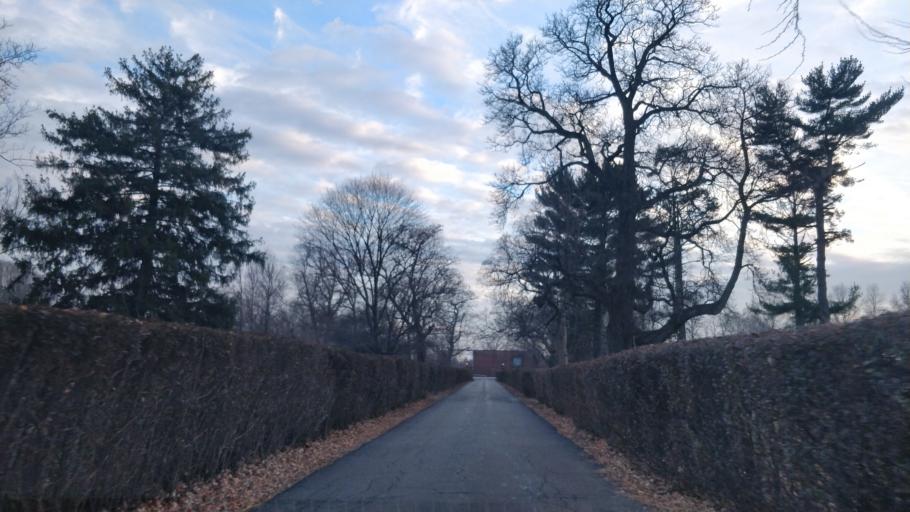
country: US
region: New York
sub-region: Nassau County
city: Glen Cove
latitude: 40.8851
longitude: -73.6284
